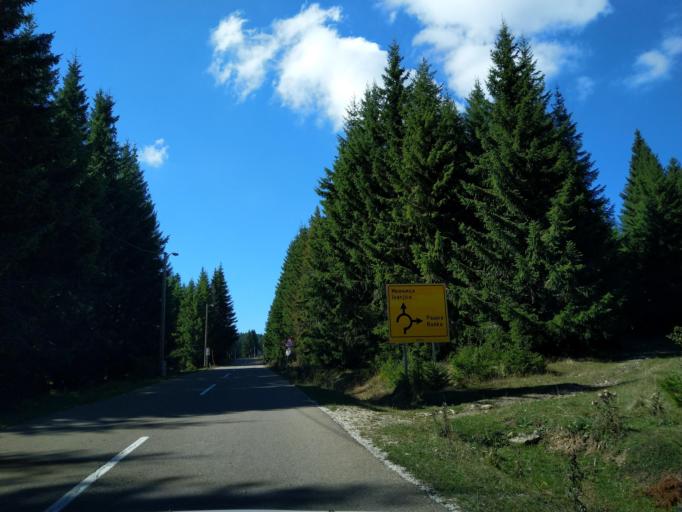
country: RS
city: Sokolovica
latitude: 43.2757
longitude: 20.3473
